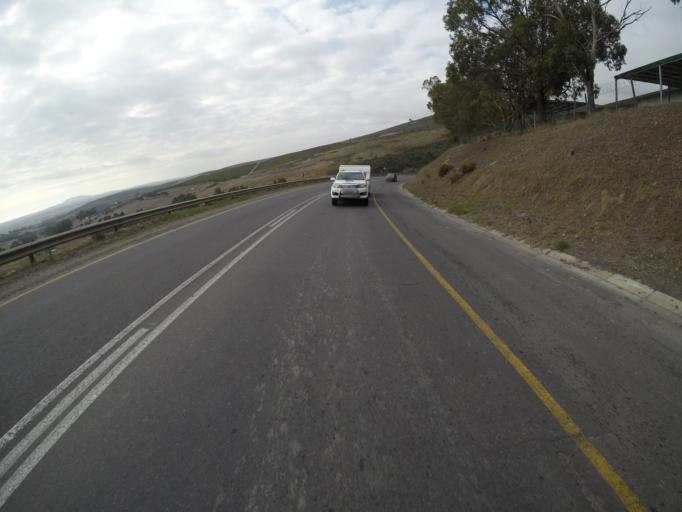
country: ZA
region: Western Cape
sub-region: City of Cape Town
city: Sunset Beach
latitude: -33.8285
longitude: 18.5889
